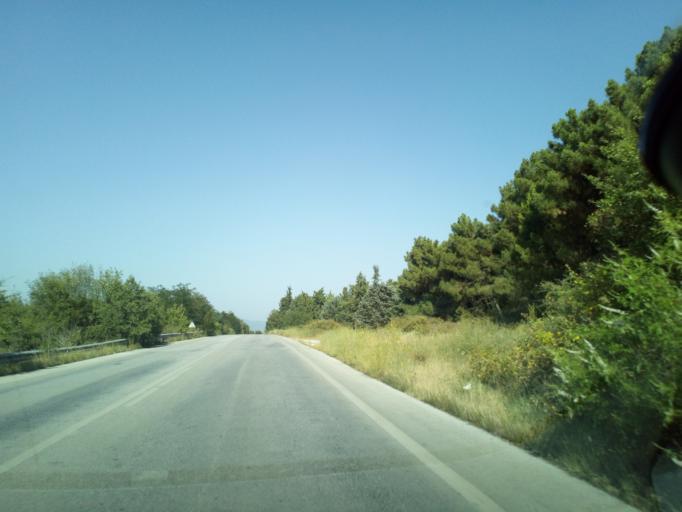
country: GR
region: Central Macedonia
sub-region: Nomos Thessalonikis
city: Nea Apollonia
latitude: 40.6600
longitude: 23.3675
